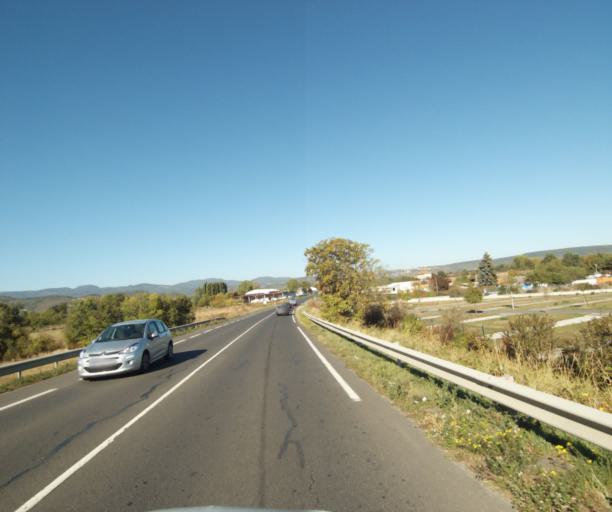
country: FR
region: Auvergne
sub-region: Departement du Puy-de-Dome
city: Gerzat
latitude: 45.8233
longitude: 3.1358
